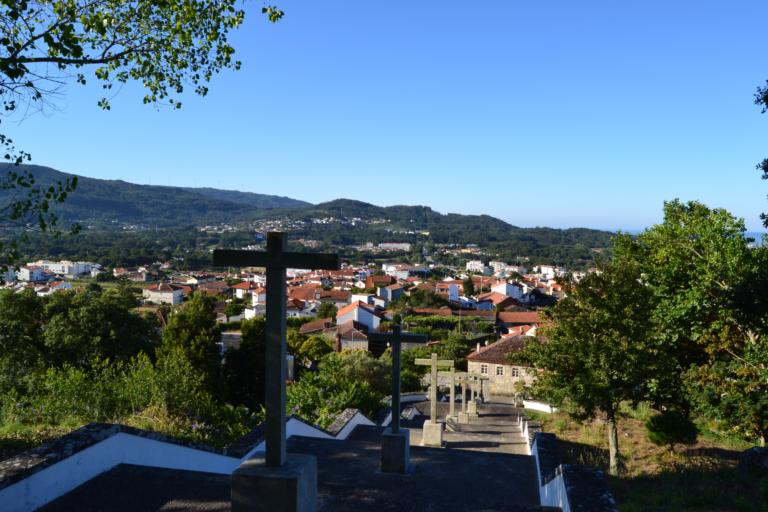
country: PT
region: Viana do Castelo
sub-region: Caminha
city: Vila Praia de Ancora
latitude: 41.8162
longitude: -8.8537
